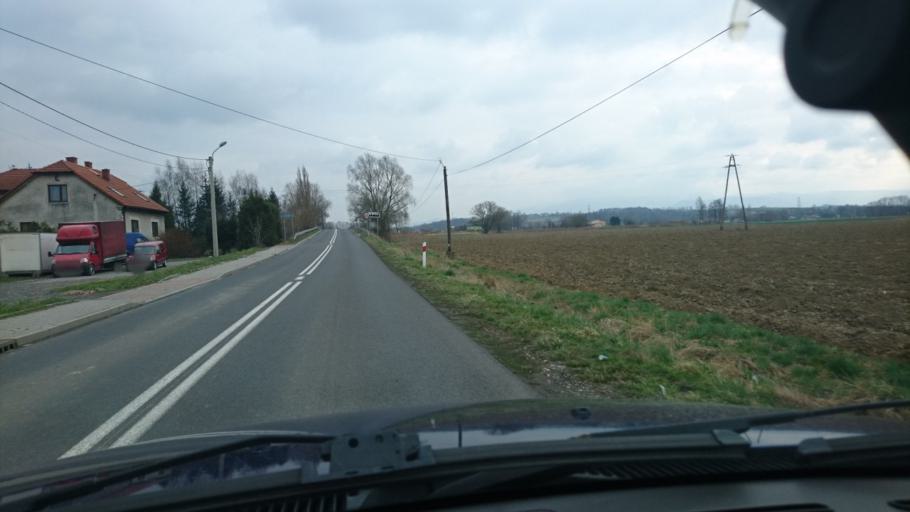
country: PL
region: Silesian Voivodeship
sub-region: Powiat bielski
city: Ligota
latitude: 49.8756
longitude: 18.9544
